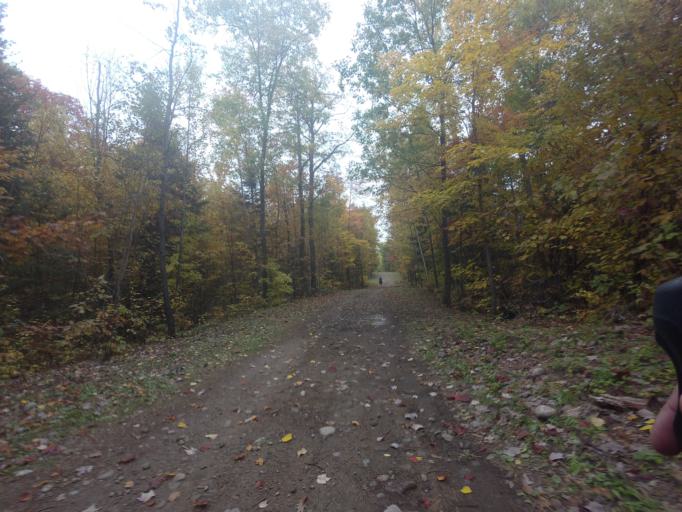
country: CA
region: Ontario
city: Petawawa
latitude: 45.7573
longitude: -77.3628
